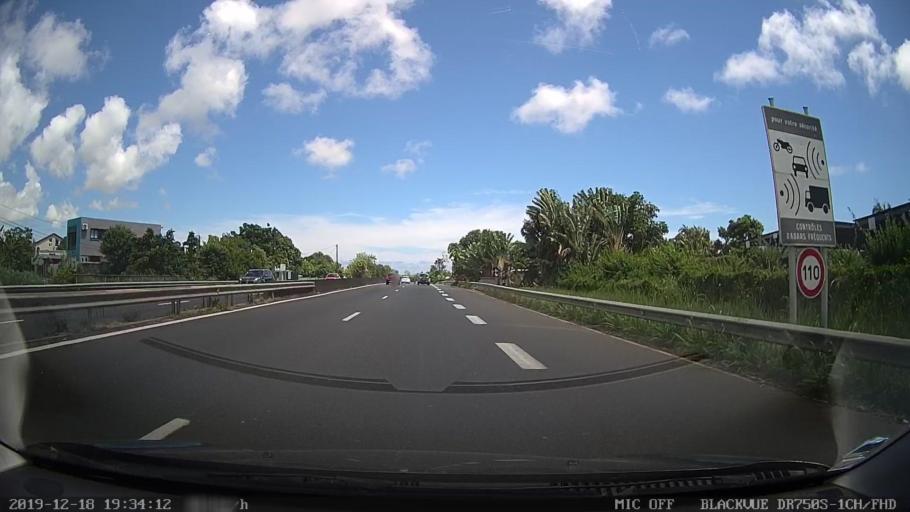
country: RE
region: Reunion
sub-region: Reunion
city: Saint-Andre
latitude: -20.9592
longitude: 55.6576
